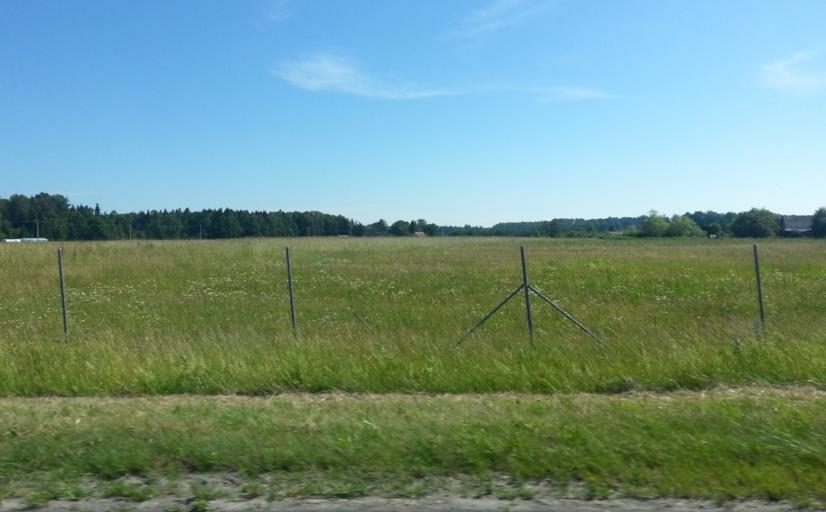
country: LT
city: Sirvintos
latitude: 55.0872
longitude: 24.8679
